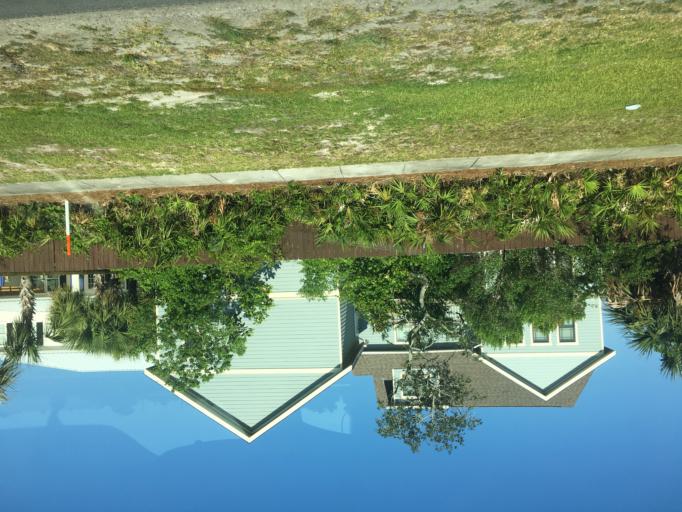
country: US
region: Florida
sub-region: Bay County
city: Panama City Beach
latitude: 30.2010
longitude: -85.8361
